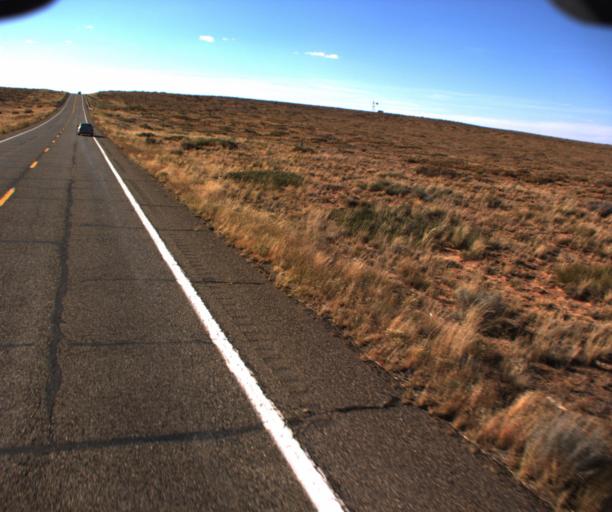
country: US
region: Arizona
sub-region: Coconino County
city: Kaibito
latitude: 36.6122
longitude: -111.0252
